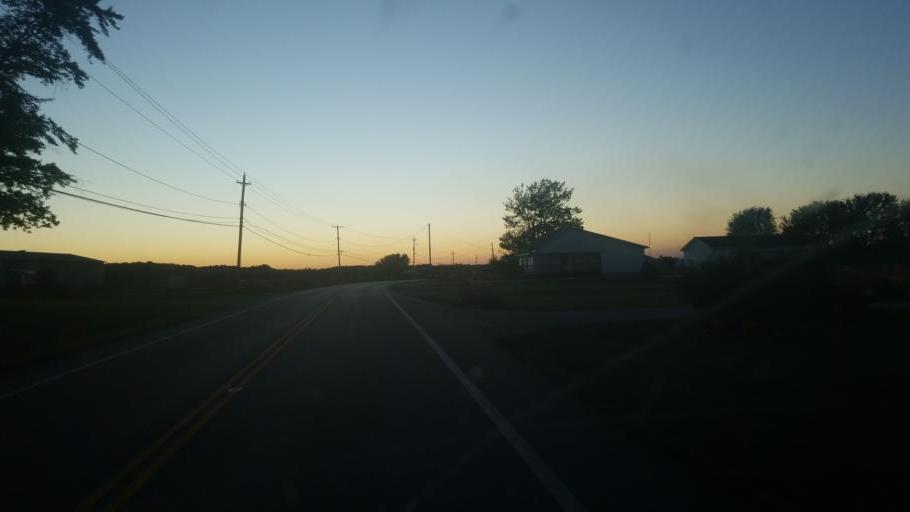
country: US
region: Ohio
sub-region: Ashtabula County
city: Andover
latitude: 41.7512
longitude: -80.6021
